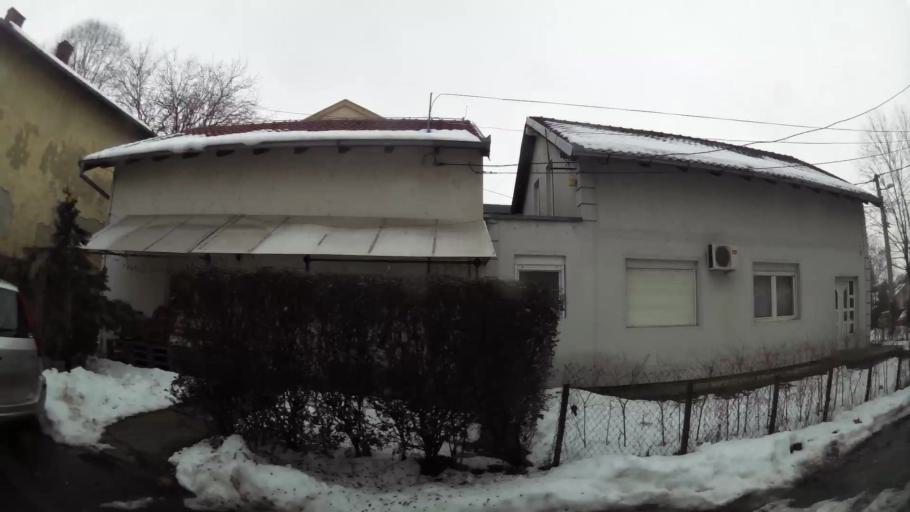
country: RS
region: Central Serbia
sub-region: Belgrade
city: Zemun
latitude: 44.8568
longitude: 20.3778
